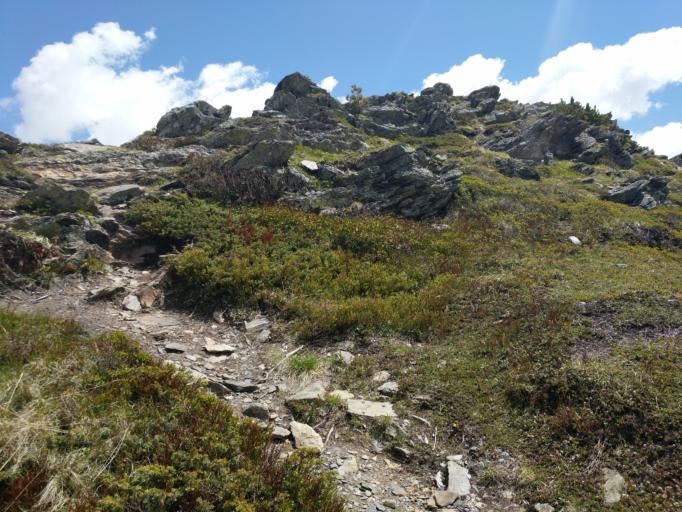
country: FR
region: Rhone-Alpes
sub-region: Departement de la Haute-Savoie
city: Chamonix-Mont-Blanc
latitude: 46.0188
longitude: 6.9394
